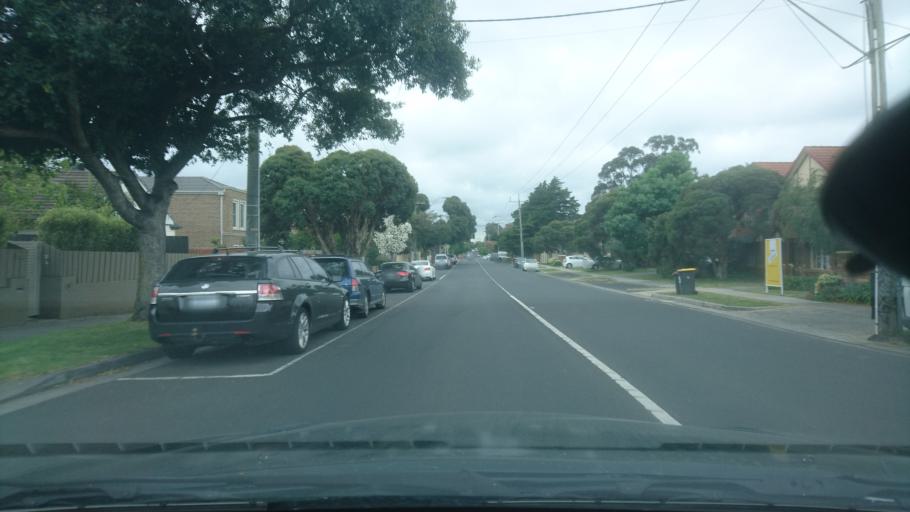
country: AU
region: Victoria
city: Murrumbeena
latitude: -37.9075
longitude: 145.0743
